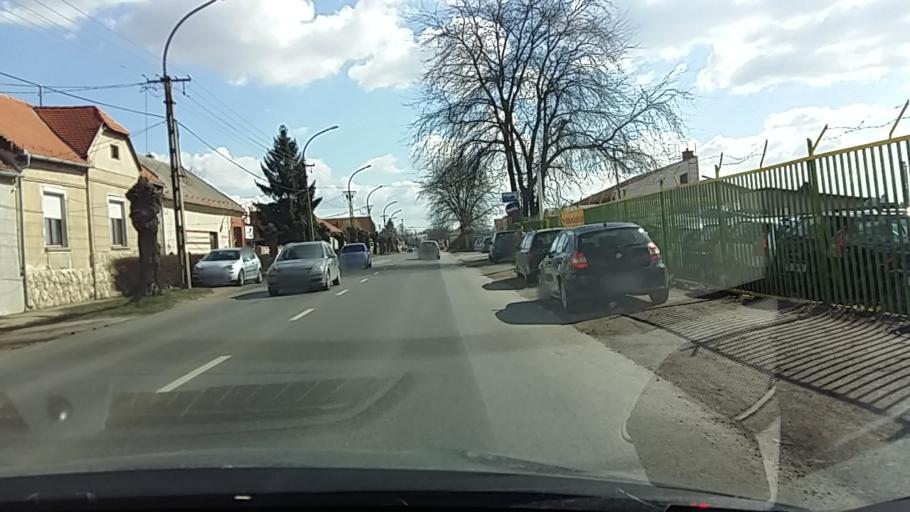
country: HU
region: Baranya
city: Pecs
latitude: 46.0786
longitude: 18.2619
